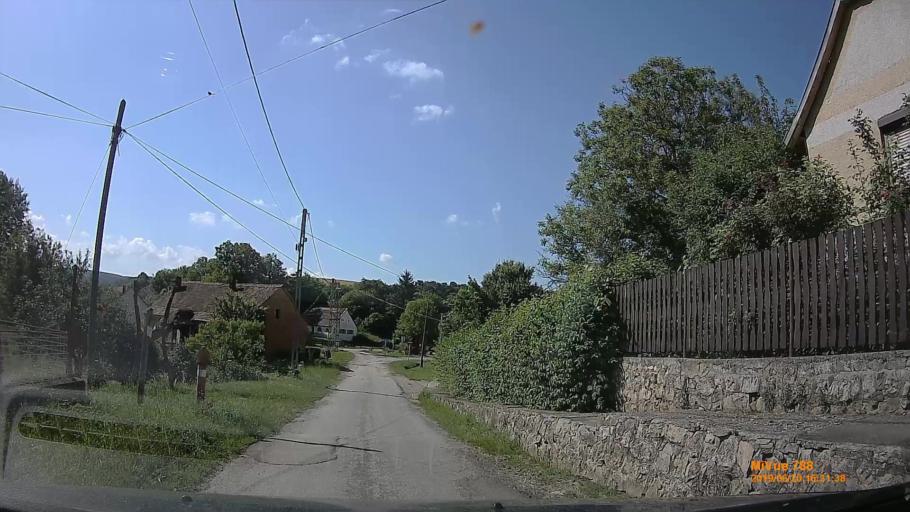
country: HU
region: Baranya
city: Buekkoesd
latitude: 46.1721
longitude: 18.0509
